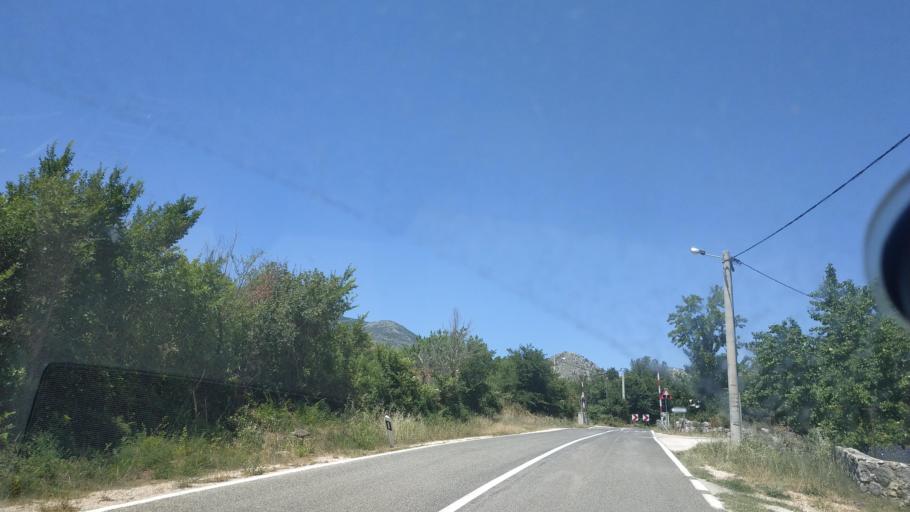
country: HR
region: Sibensko-Kniniska
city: Drnis
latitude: 43.8889
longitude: 16.2083
